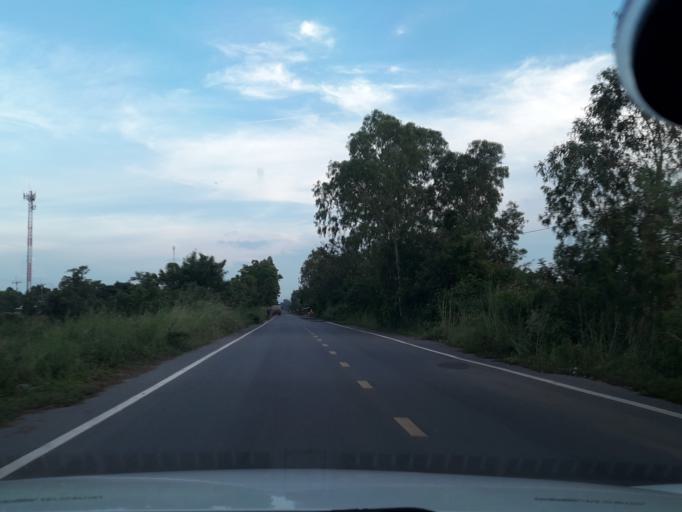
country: TH
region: Sara Buri
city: Nong Khae
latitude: 14.3092
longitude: 100.8861
